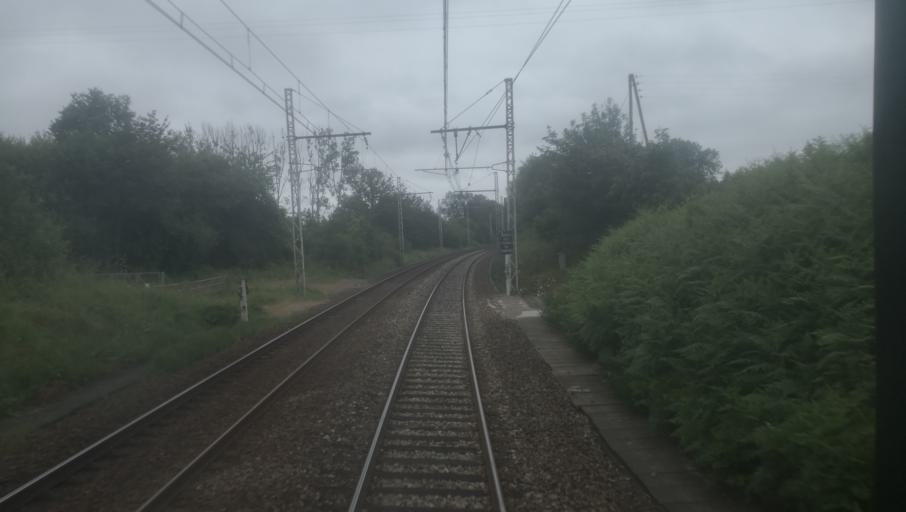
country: FR
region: Centre
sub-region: Departement de l'Indre
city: Chantome
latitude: 46.4351
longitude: 1.5534
